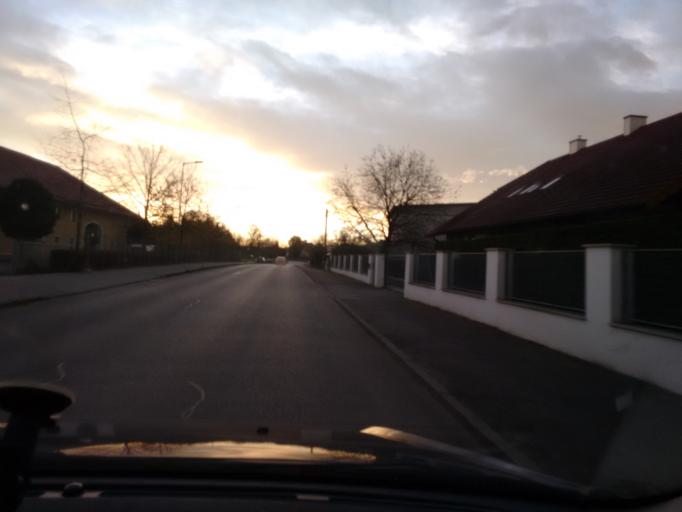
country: AT
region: Upper Austria
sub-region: Wels Stadt
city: Wels
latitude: 48.1775
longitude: 14.0123
